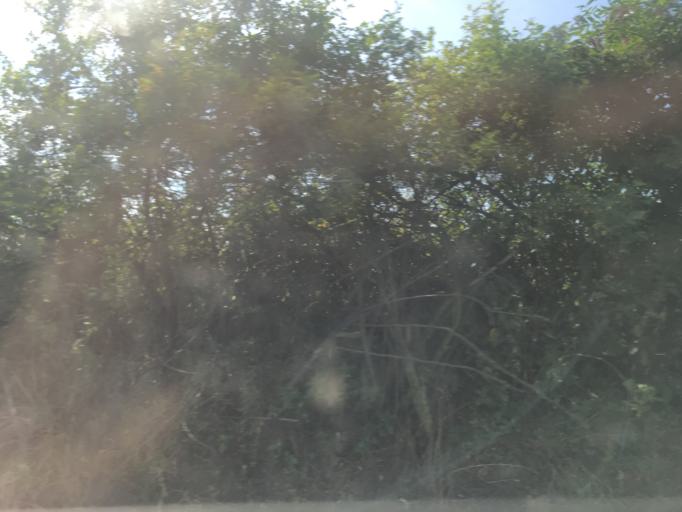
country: CZ
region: Jihocesky
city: Chotoviny
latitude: 49.5366
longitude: 14.6387
